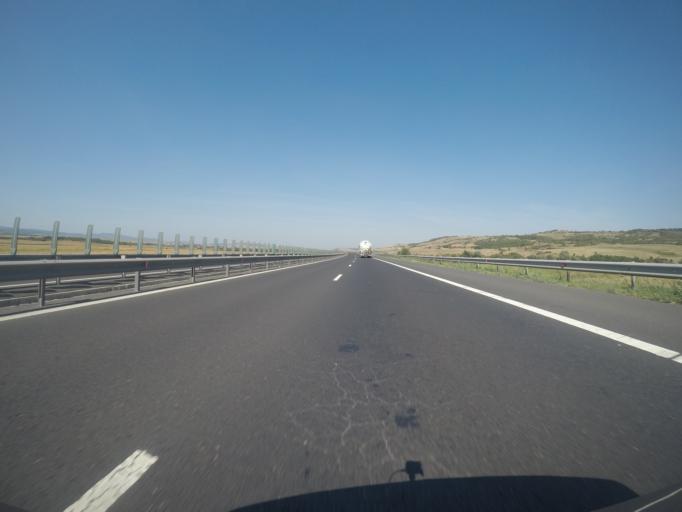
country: RO
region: Sibiu
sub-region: Comuna Apoldu de Jos
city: Apoldu de Jos
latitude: 45.8893
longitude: 23.8413
